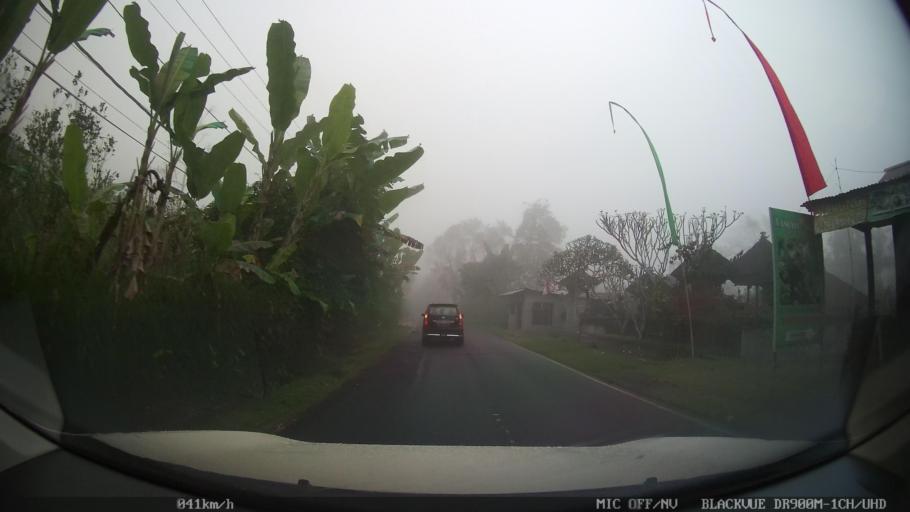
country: ID
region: Bali
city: Banjar Taro Kelod
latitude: -8.3297
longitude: 115.2883
